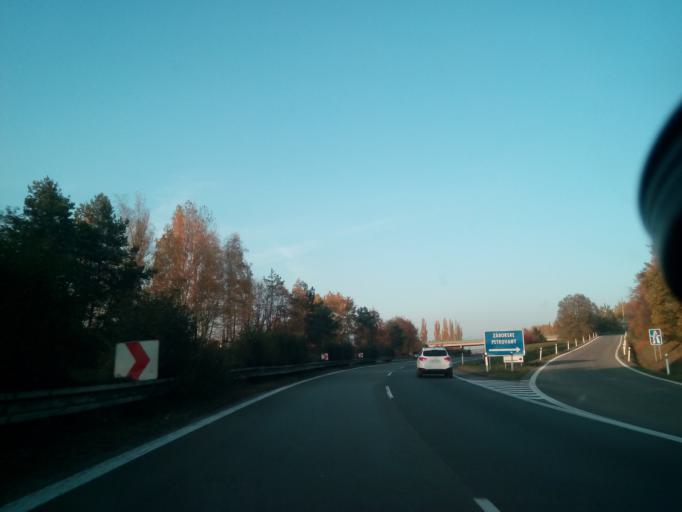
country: SK
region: Presovsky
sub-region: Okres Presov
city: Presov
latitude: 48.9504
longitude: 21.2552
